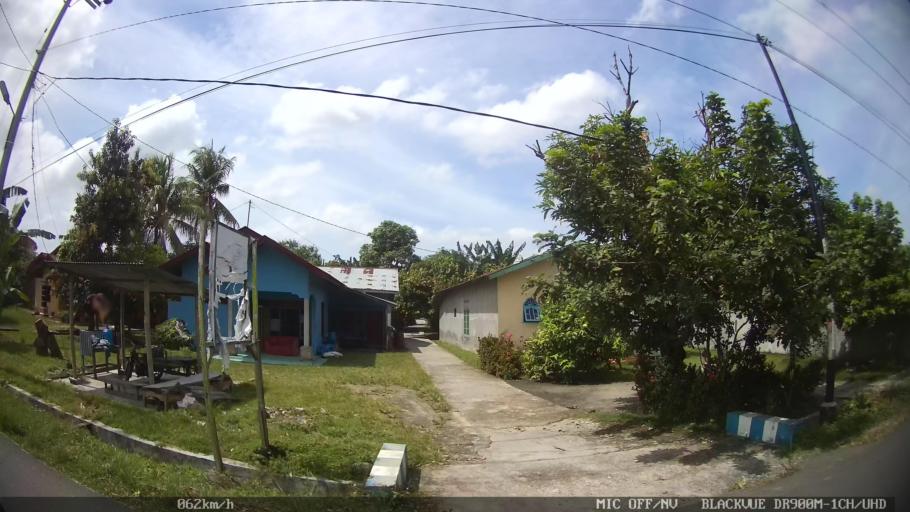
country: ID
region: North Sumatra
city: Percut
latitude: 3.5893
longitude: 98.8640
